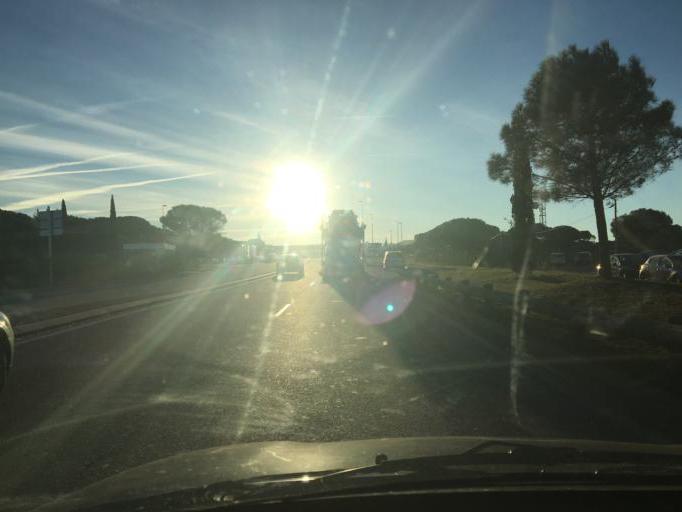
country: FR
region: Provence-Alpes-Cote d'Azur
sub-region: Departement du Var
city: Le Muy
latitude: 43.4624
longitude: 6.5485
